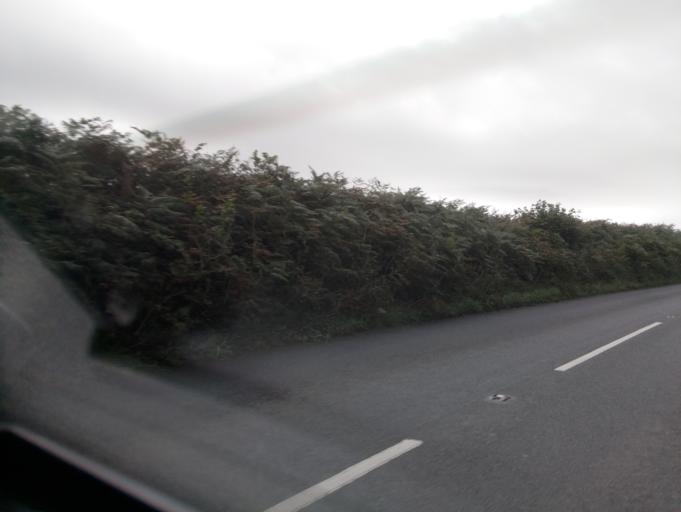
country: GB
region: England
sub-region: Devon
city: Kingsbridge
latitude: 50.2925
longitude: -3.7858
